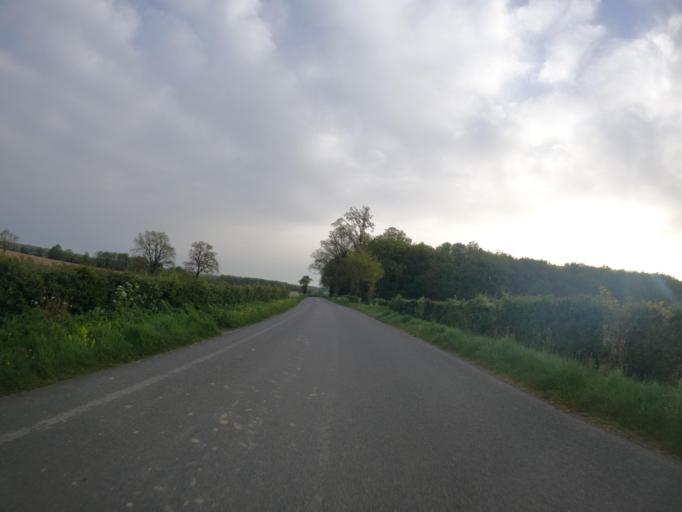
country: FR
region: Poitou-Charentes
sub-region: Departement des Deux-Sevres
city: Moncoutant
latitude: 46.6970
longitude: -0.5372
